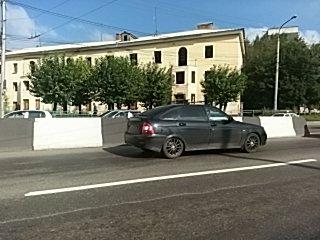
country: RU
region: Krasnoyarskiy
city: Solnechnyy
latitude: 56.0420
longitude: 92.9404
